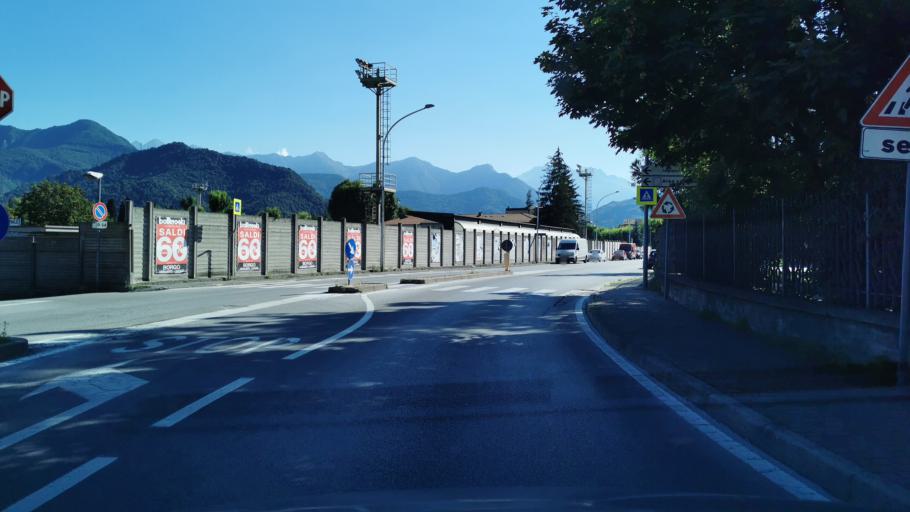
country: IT
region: Piedmont
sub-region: Provincia di Cuneo
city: Borgo San Dalmazzo
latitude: 44.3299
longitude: 7.4910
